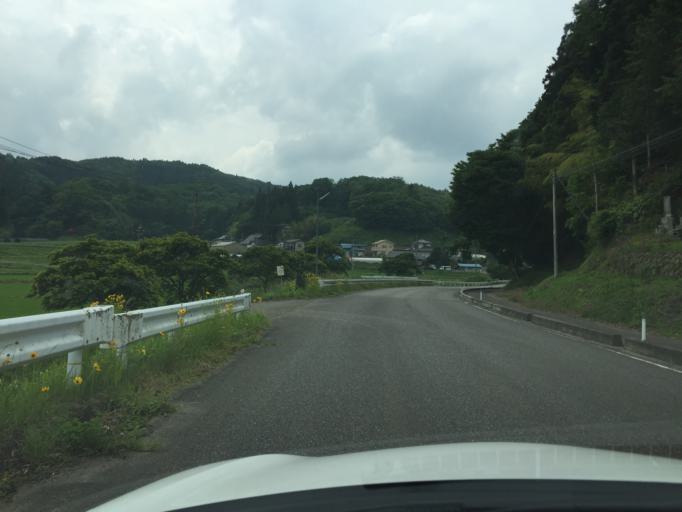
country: JP
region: Fukushima
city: Funehikimachi-funehiki
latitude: 37.2945
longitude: 140.5793
